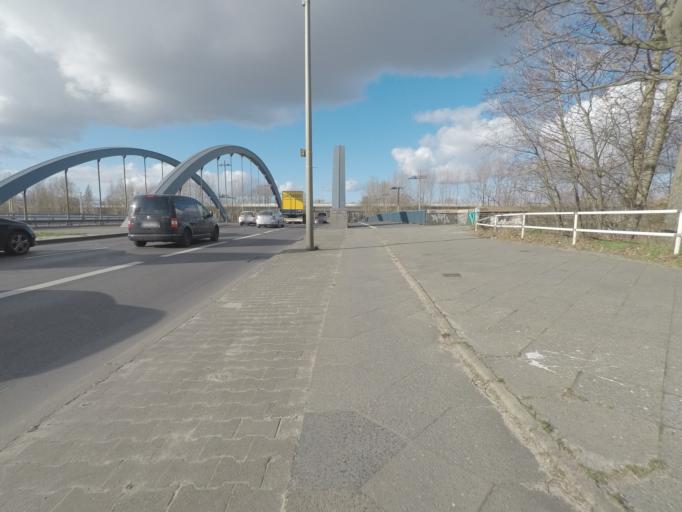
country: DE
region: Berlin
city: Charlottenburg-Nord
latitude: 52.5322
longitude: 13.2952
